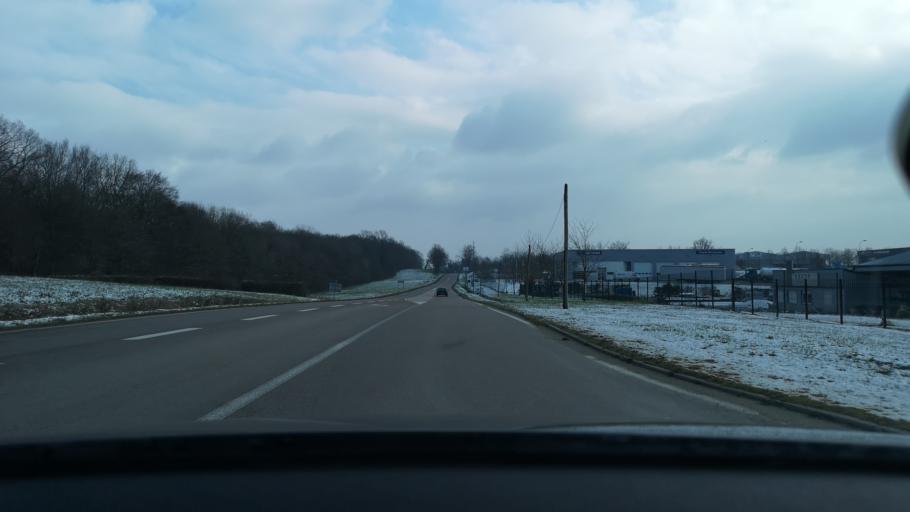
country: FR
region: Franche-Comte
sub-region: Departement du Jura
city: Bletterans
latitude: 46.6696
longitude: 5.4079
